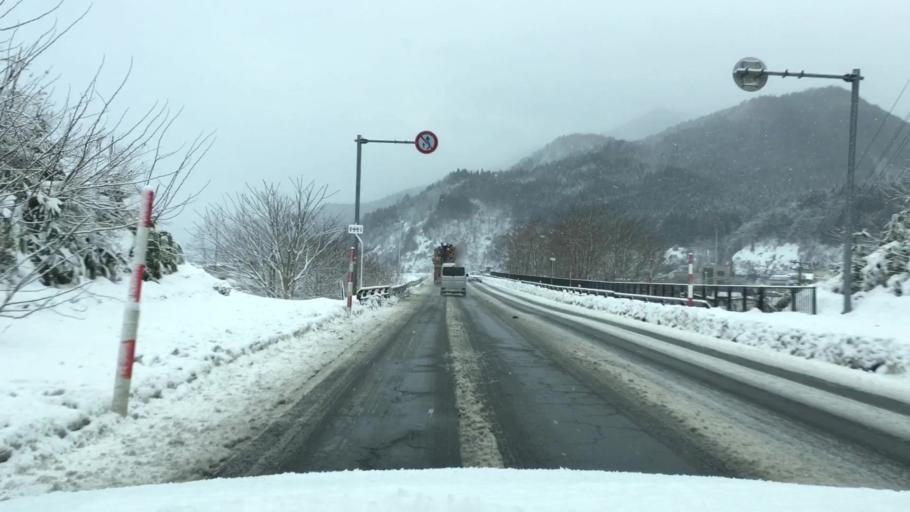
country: JP
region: Aomori
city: Kuroishi
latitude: 40.5237
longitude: 140.5811
